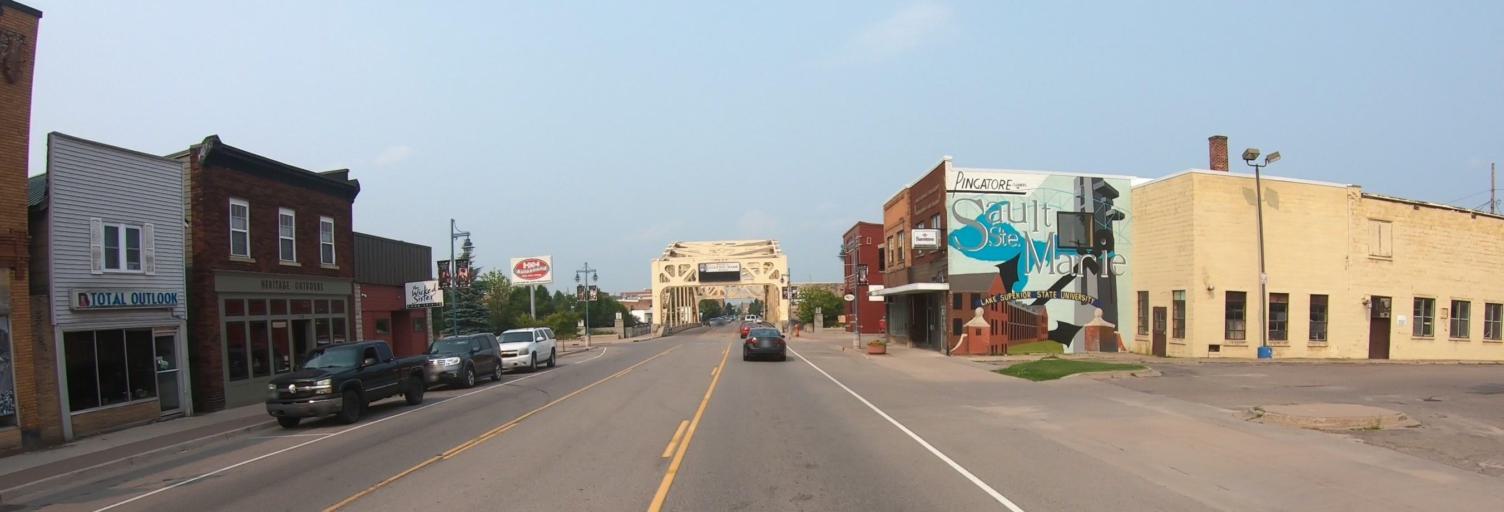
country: US
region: Michigan
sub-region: Chippewa County
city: Sault Ste. Marie
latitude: 46.4943
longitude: -84.3502
